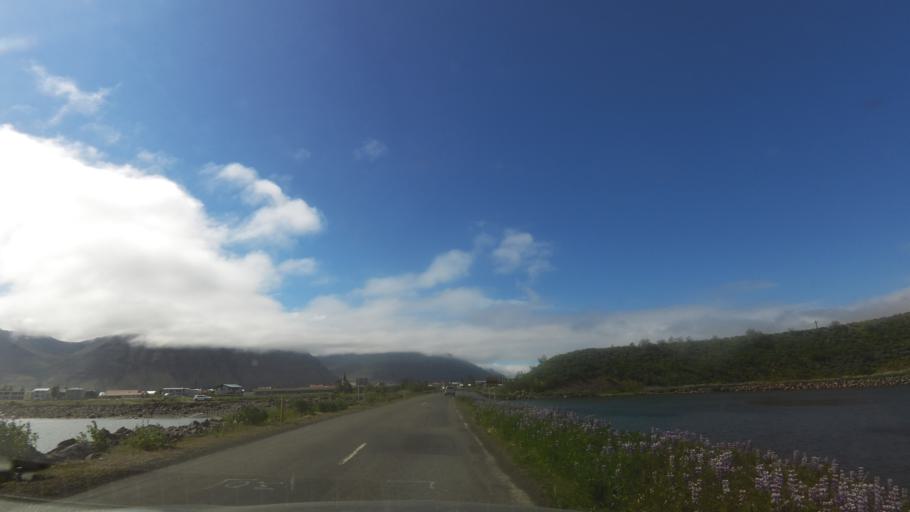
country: IS
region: Westfjords
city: Isafjoerdur
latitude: 66.0513
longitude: -23.5053
